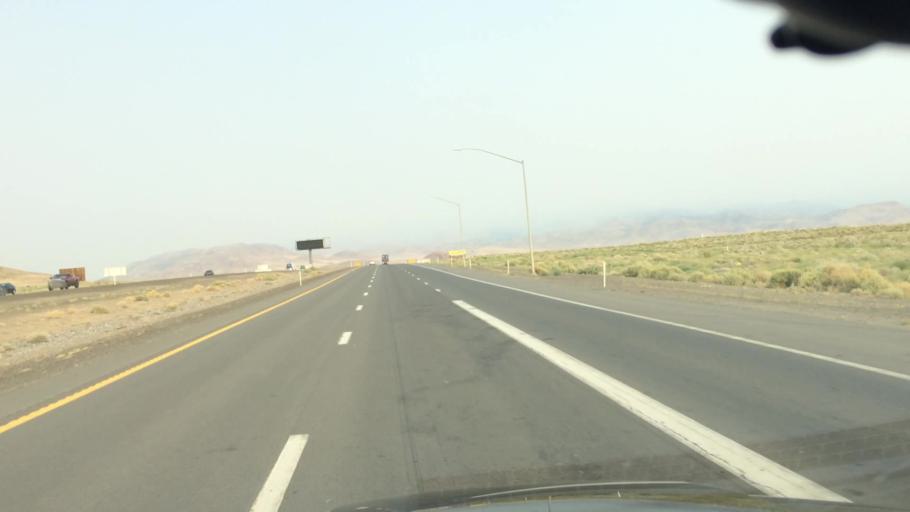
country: US
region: Nevada
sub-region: Lyon County
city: Fernley
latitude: 39.6170
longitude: -119.2704
